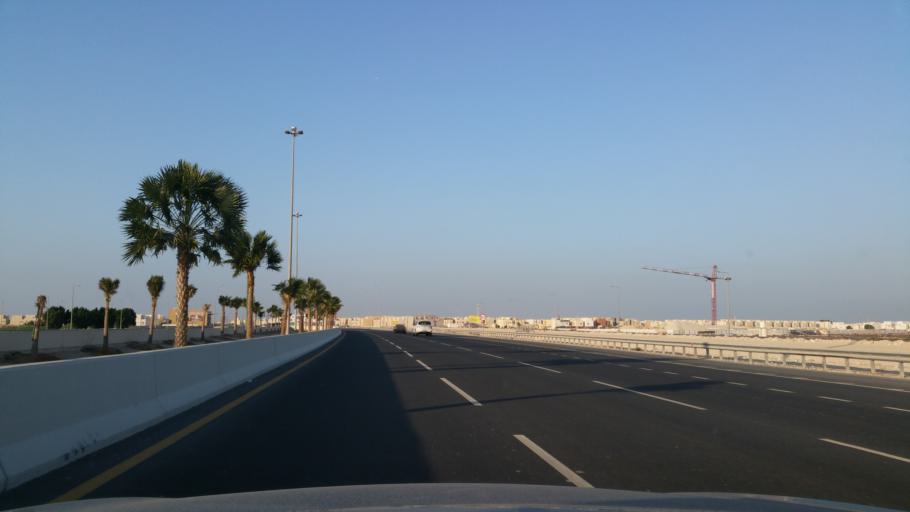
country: QA
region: Al Khawr
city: Al Khawr
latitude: 25.6593
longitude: 51.5003
